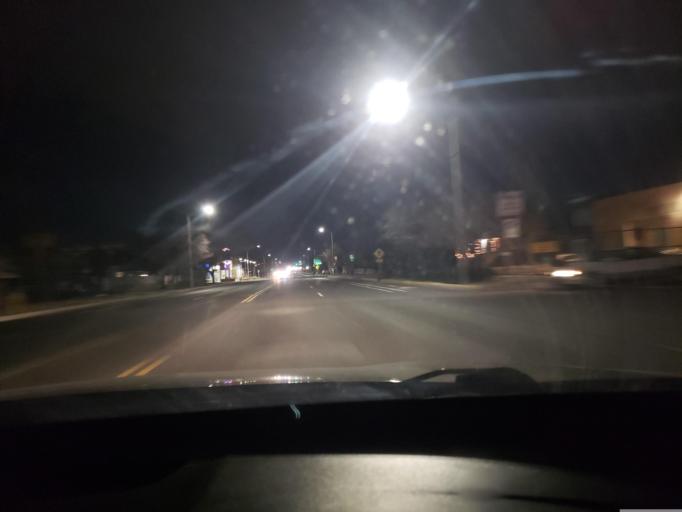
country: US
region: New Mexico
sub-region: Bernalillo County
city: Albuquerque
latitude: 35.0714
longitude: -106.6456
